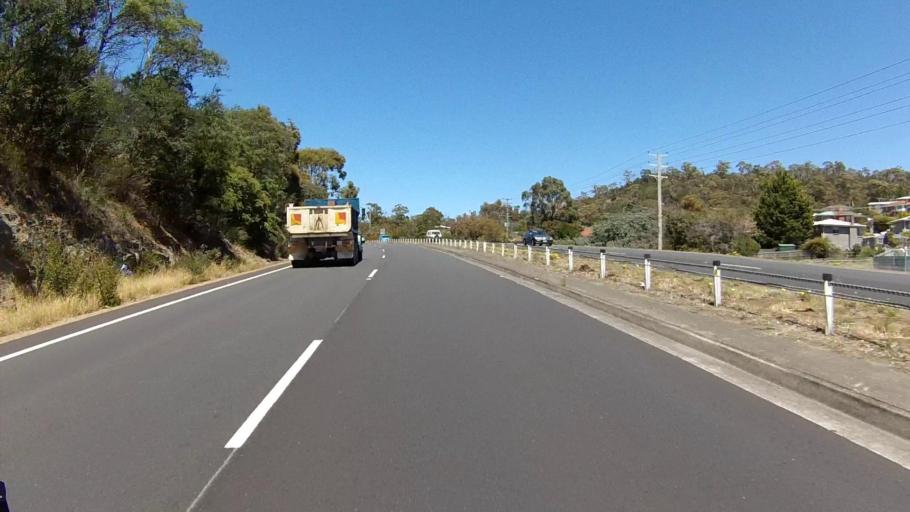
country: AU
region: Tasmania
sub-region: Clarence
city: Warrane
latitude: -42.8625
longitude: 147.3934
